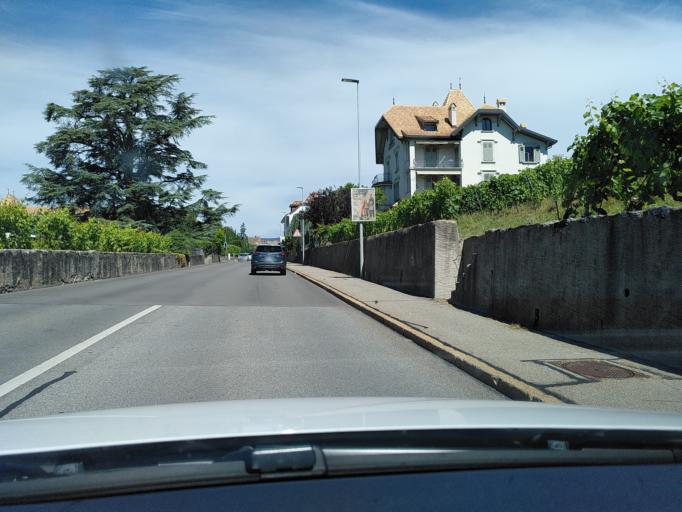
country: CH
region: Vaud
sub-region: Morges District
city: Aubonne
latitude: 46.4921
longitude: 6.3951
